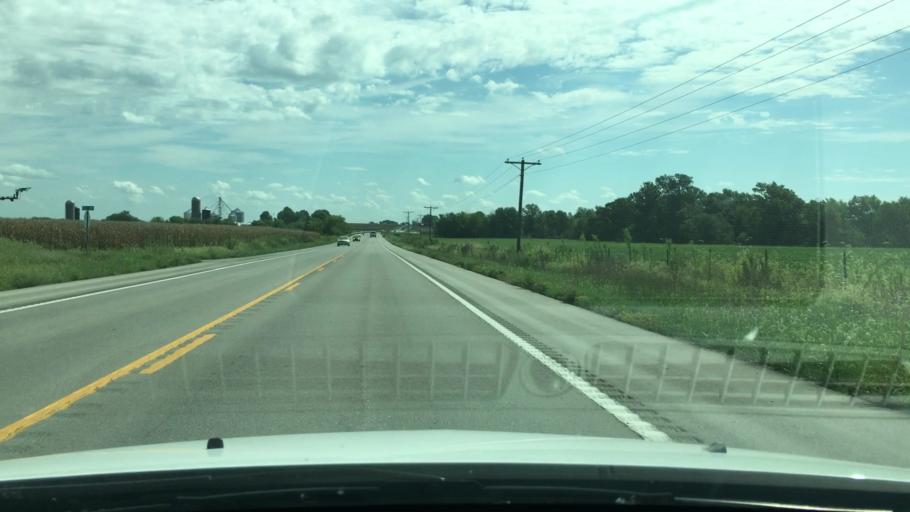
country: US
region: Missouri
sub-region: Montgomery County
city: Wellsville
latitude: 39.1644
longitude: -91.7099
